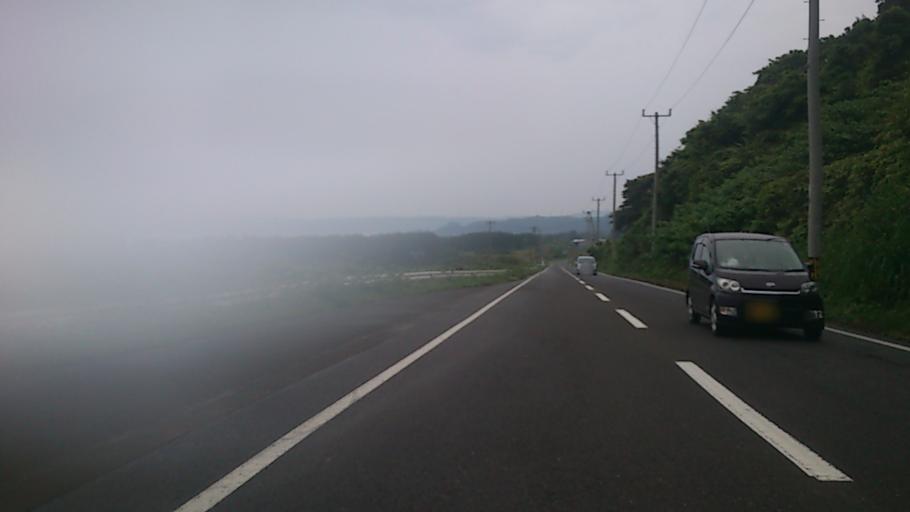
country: JP
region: Akita
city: Noshiromachi
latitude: 40.5218
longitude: 139.9507
